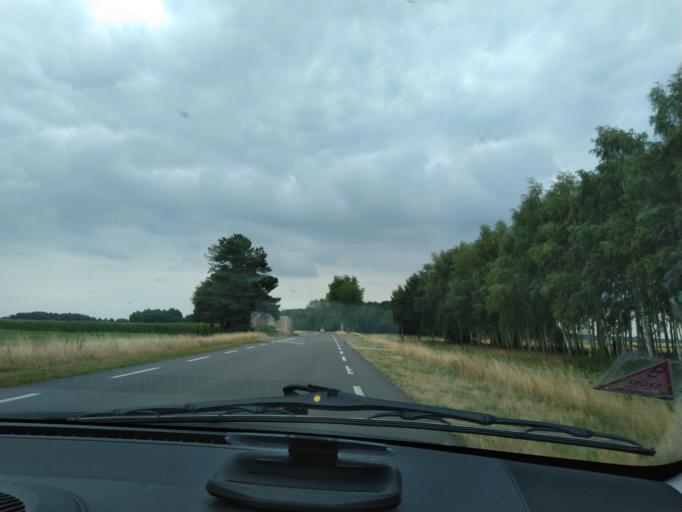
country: DE
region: Lower Saxony
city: Rhede
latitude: 53.0741
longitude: 7.1938
